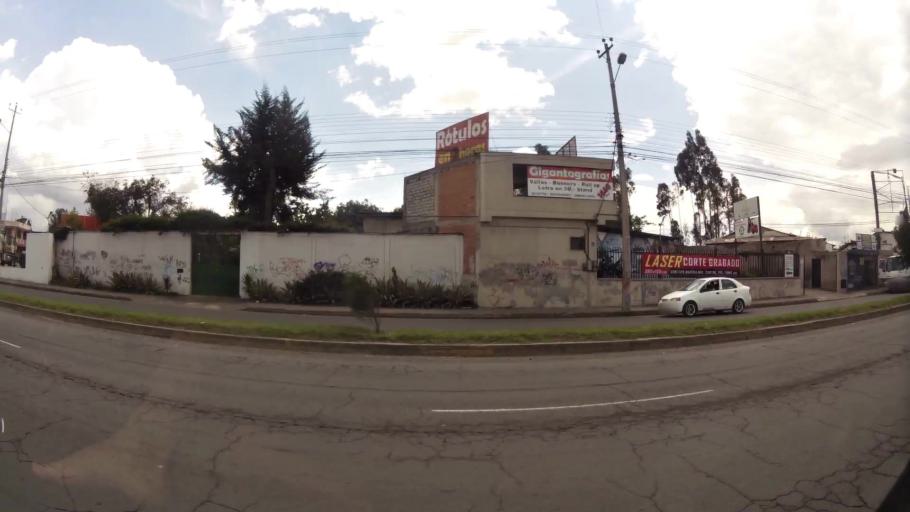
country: EC
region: Pichincha
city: Quito
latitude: -0.1051
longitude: -78.4319
